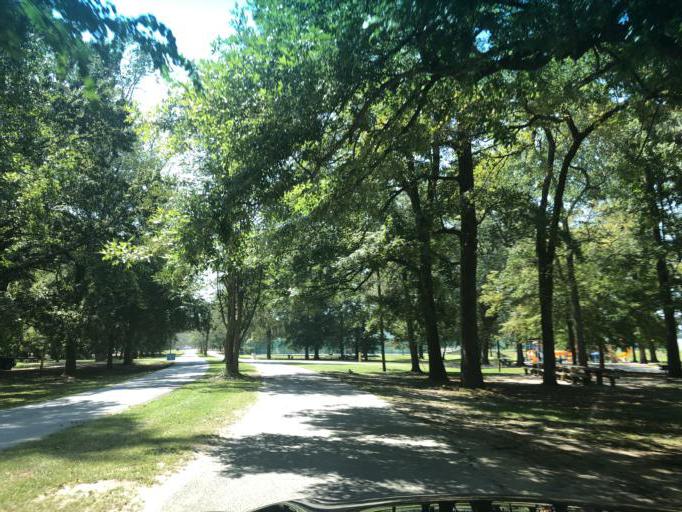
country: US
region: Georgia
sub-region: Muscogee County
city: Columbus
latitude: 32.5142
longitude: -84.9086
